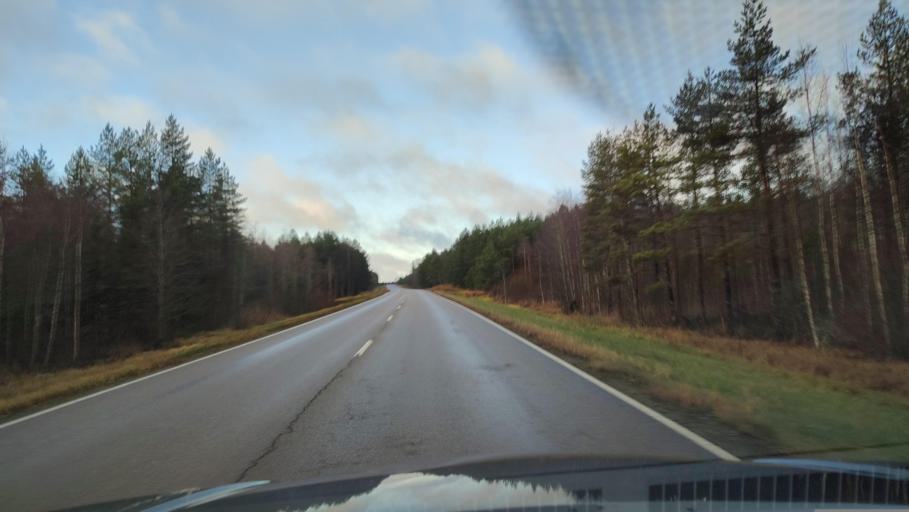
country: FI
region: Ostrobothnia
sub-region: Sydosterbotten
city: Kristinestad
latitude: 62.3016
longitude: 21.4119
